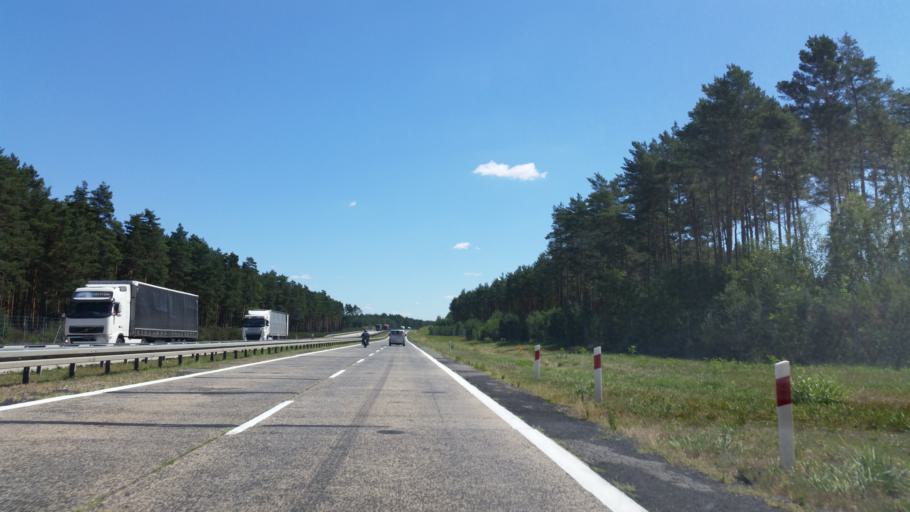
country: PL
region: Lubusz
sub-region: Powiat zaganski
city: Malomice
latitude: 51.4205
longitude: 15.4672
